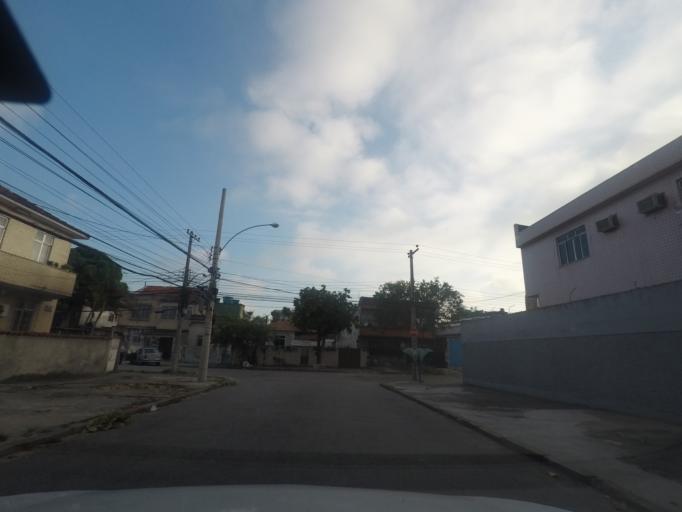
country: BR
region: Rio de Janeiro
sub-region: Duque De Caxias
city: Duque de Caxias
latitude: -22.8342
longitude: -43.2783
